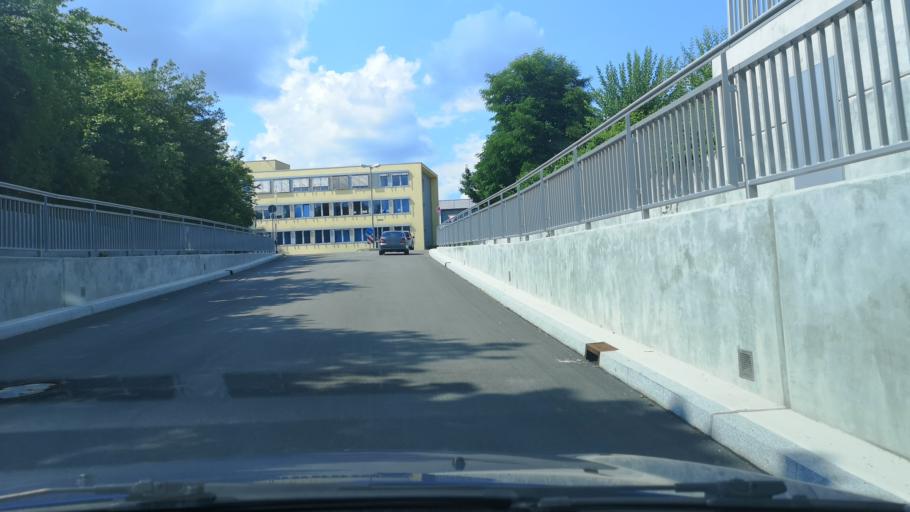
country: DE
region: Bavaria
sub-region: Upper Bavaria
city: Poing
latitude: 48.1693
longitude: 11.8013
